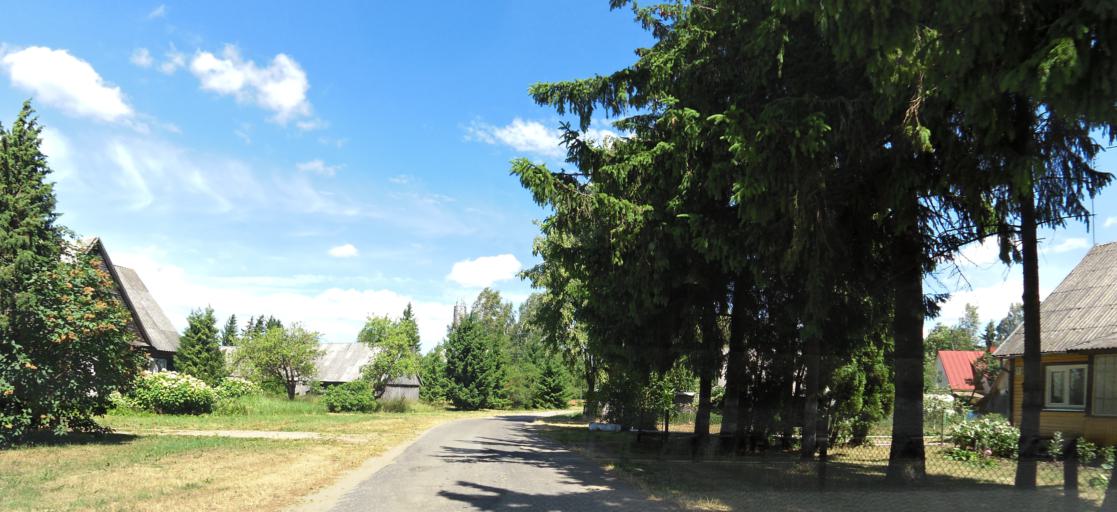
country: LT
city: Kupiskis
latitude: 55.9718
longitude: 24.9957
